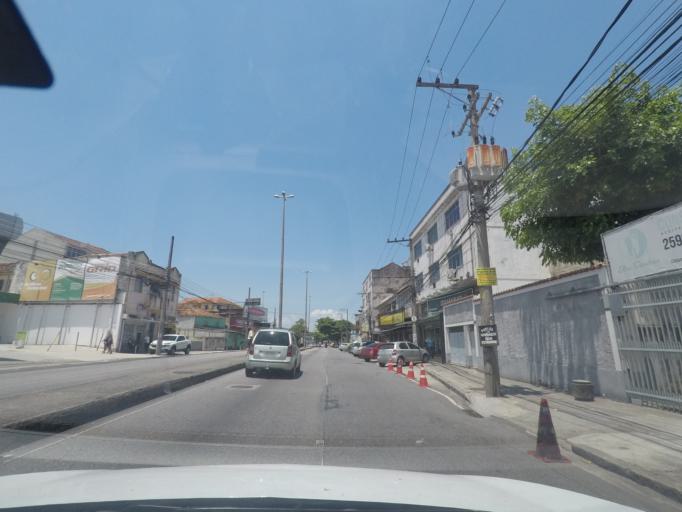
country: BR
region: Rio de Janeiro
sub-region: Rio De Janeiro
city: Rio de Janeiro
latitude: -22.8842
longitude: -43.2974
